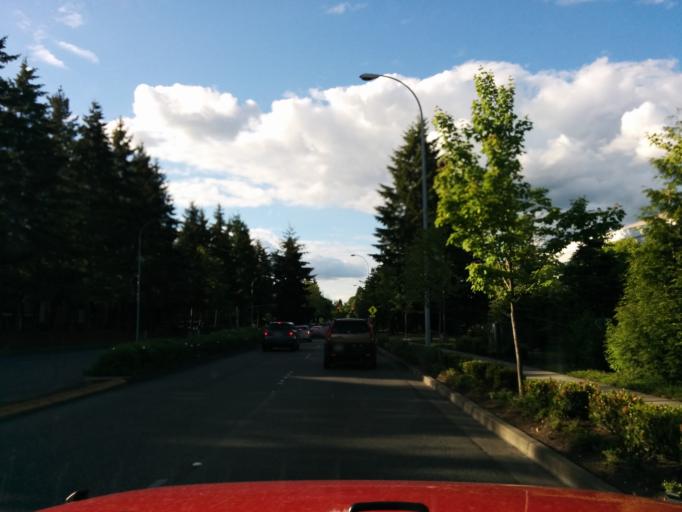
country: US
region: Washington
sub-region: King County
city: Redmond
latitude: 47.6424
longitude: -122.1428
